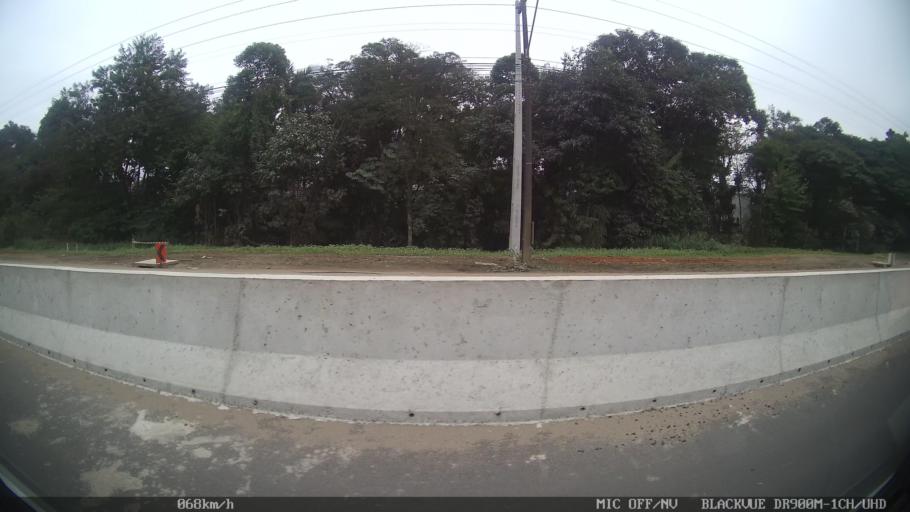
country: BR
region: Santa Catarina
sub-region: Joinville
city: Joinville
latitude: -26.2512
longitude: -48.8663
